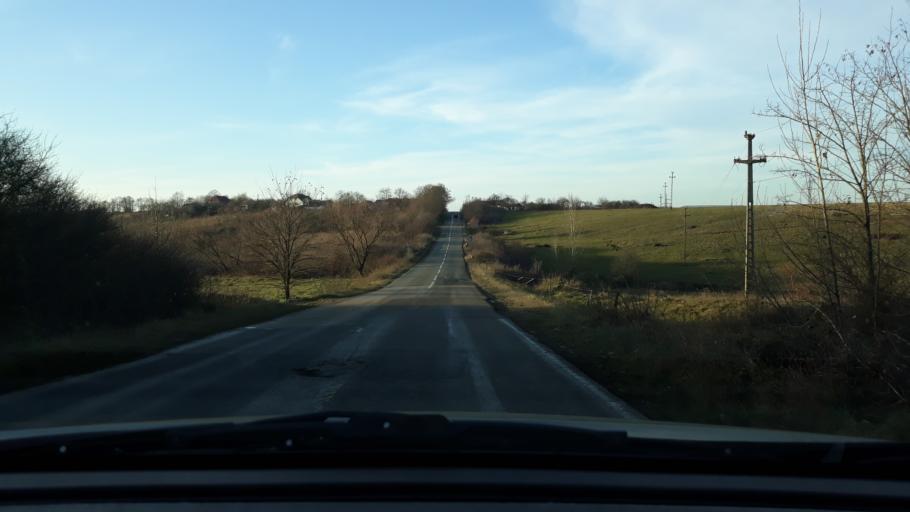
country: RO
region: Bihor
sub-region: Comuna Suplacu de Barcau
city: Suplacu de Barcau
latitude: 47.2709
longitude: 22.4940
